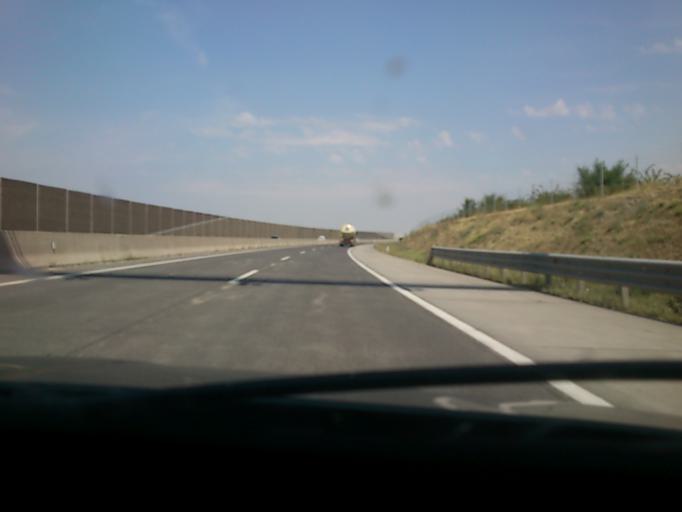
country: AT
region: Lower Austria
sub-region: Politischer Bezirk Ganserndorf
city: Aderklaa
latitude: 48.2991
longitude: 16.5094
